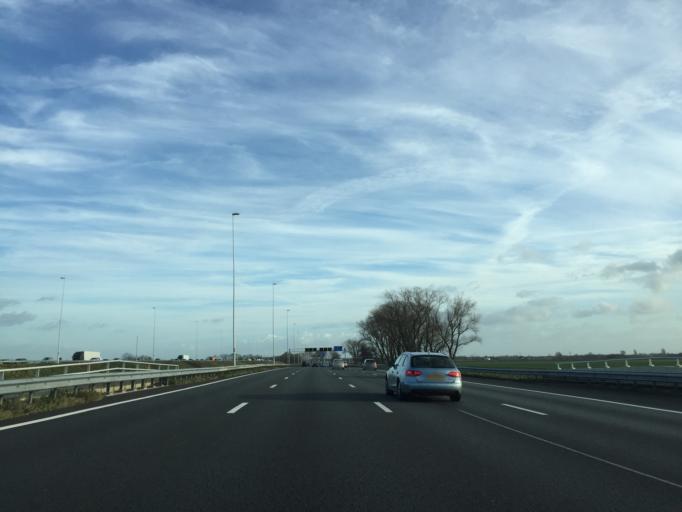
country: NL
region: South Holland
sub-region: Bodegraven-Reeuwijk
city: Bodegraven
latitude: 52.0649
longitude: 4.7918
